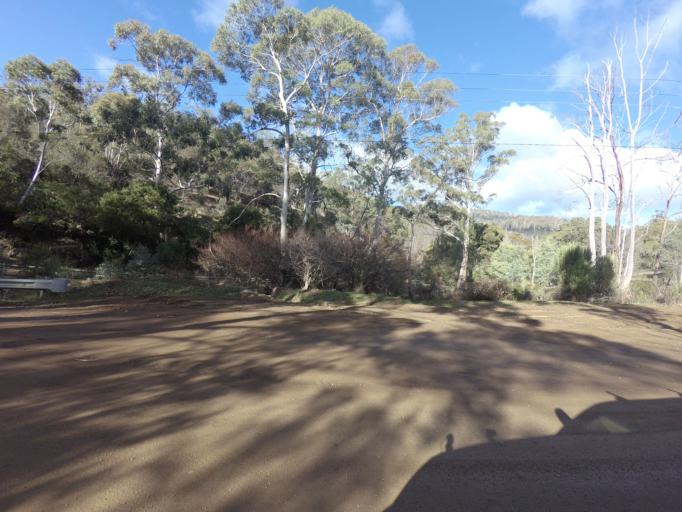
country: AU
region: Tasmania
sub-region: Derwent Valley
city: New Norfolk
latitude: -42.8165
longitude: 147.1283
